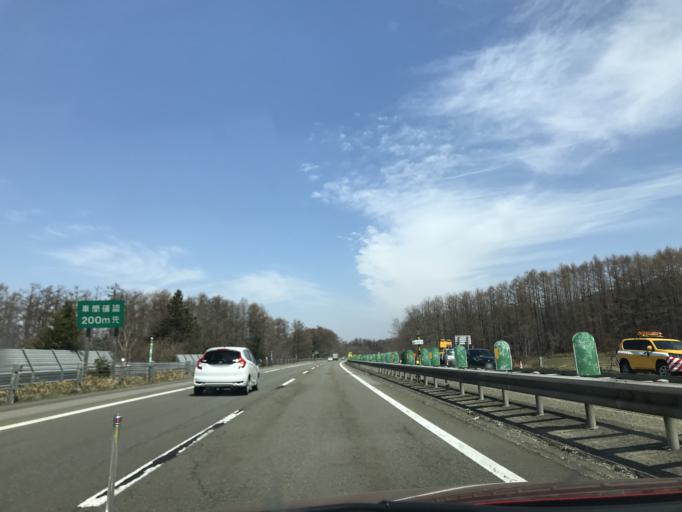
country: JP
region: Hokkaido
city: Bibai
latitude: 43.2757
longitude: 141.8502
